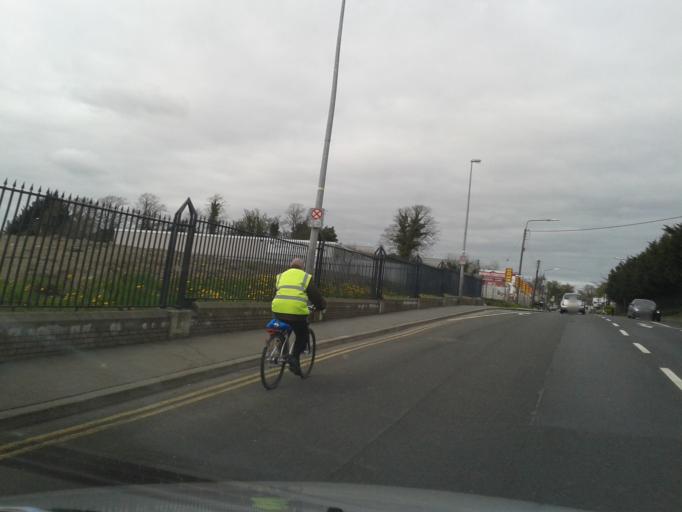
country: IE
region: Leinster
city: Beaumont
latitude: 53.3935
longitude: -6.2459
